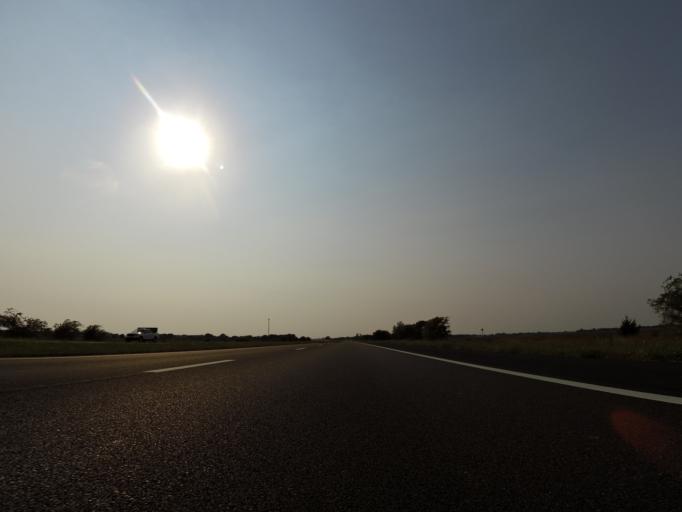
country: US
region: Kansas
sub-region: Reno County
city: Haven
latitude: 37.8919
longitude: -97.7573
